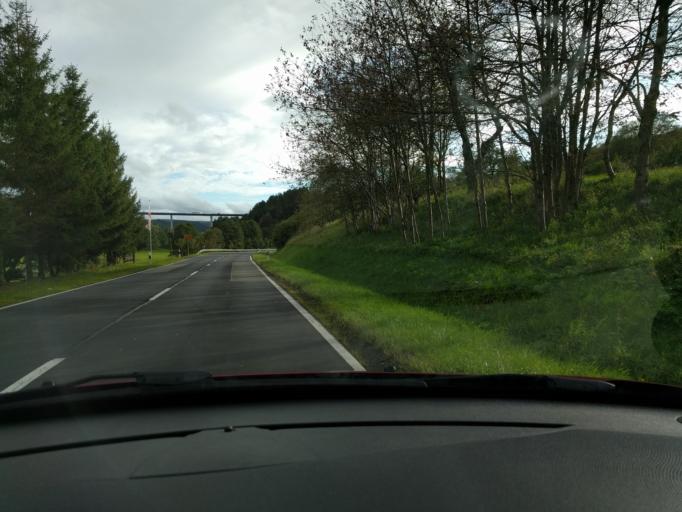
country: DE
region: Thuringia
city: Schwarza
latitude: 50.6083
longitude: 10.5221
